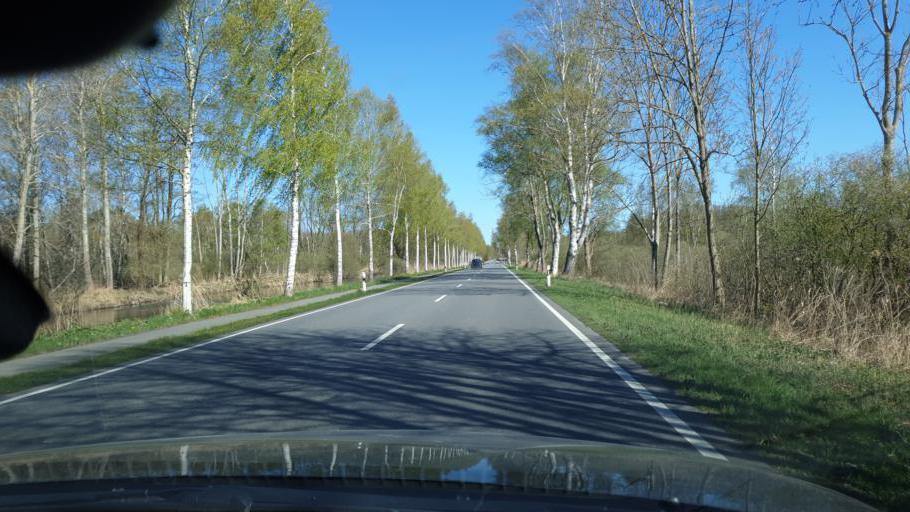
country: DE
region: Mecklenburg-Vorpommern
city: Seehof
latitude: 53.6716
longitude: 11.4493
